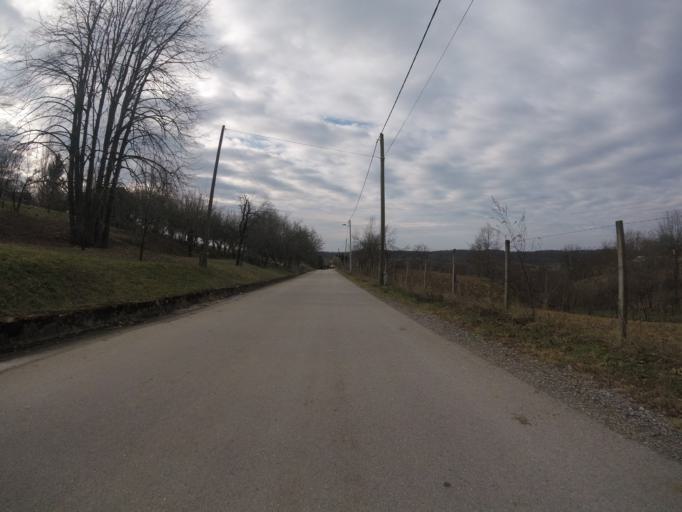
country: HR
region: Zagrebacka
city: Mraclin
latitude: 45.5131
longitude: 16.0555
